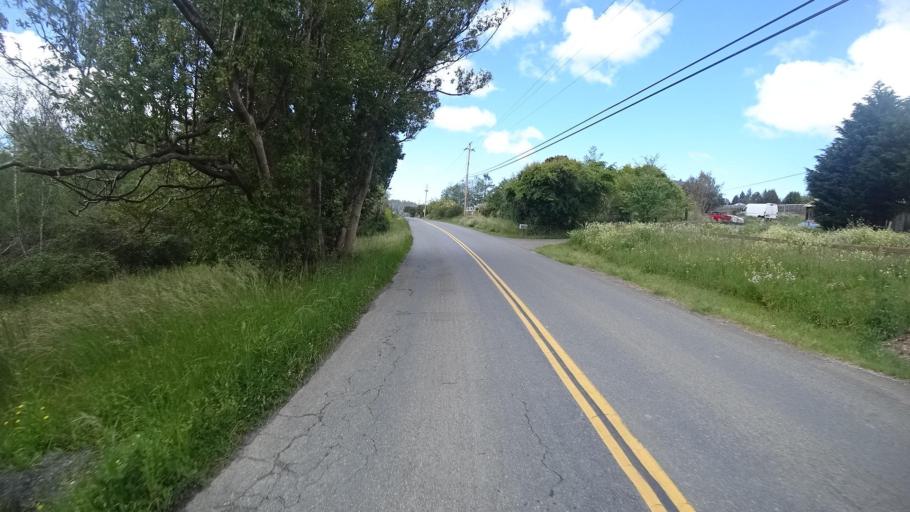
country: US
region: California
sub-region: Humboldt County
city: Blue Lake
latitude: 40.9006
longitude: -124.0114
